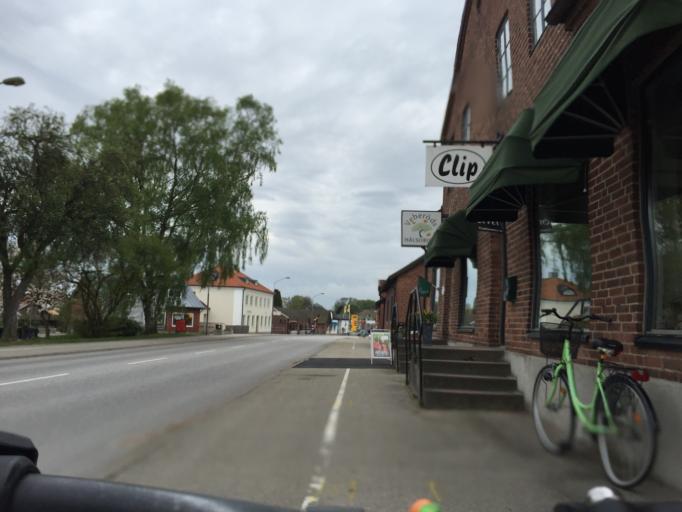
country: SE
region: Skane
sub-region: Lunds Kommun
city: Veberod
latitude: 55.6366
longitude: 13.4894
